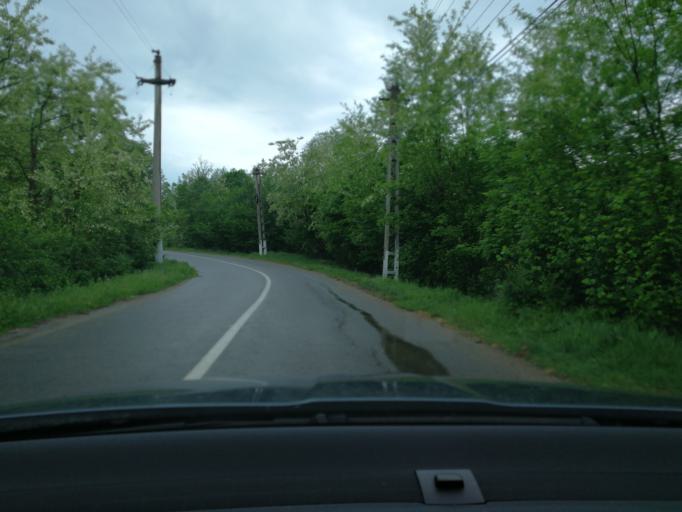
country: RO
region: Prahova
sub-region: Comuna Brebu
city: Pietriceaua
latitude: 45.2056
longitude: 25.8346
